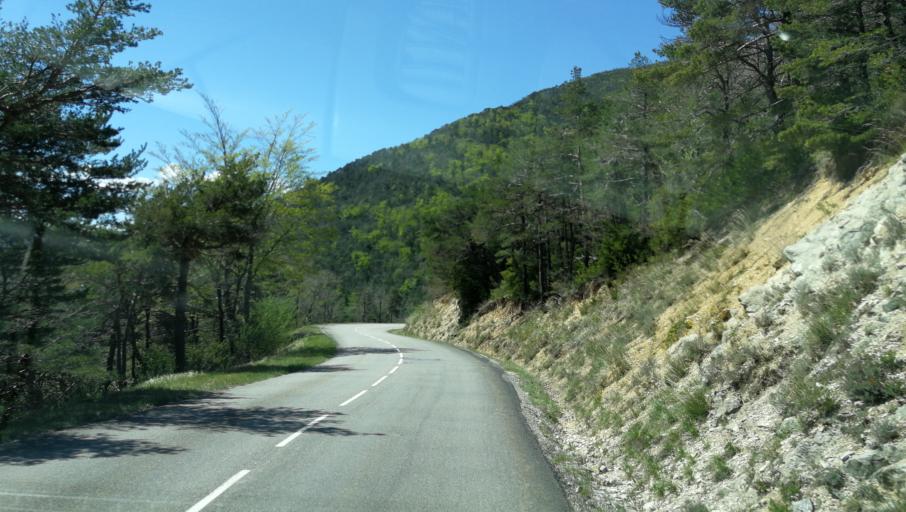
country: FR
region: Rhone-Alpes
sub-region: Departement de la Drome
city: Die
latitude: 44.8229
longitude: 5.3939
